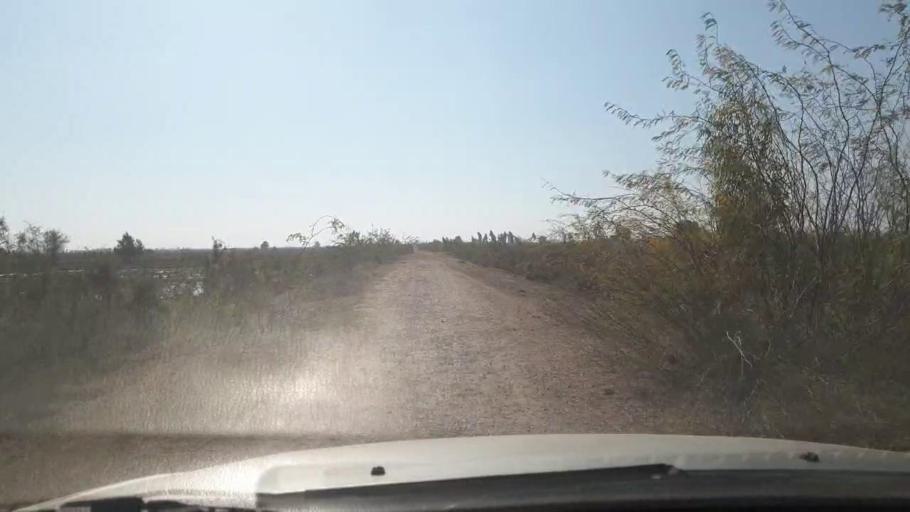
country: PK
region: Sindh
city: Adilpur
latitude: 27.8989
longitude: 69.2537
